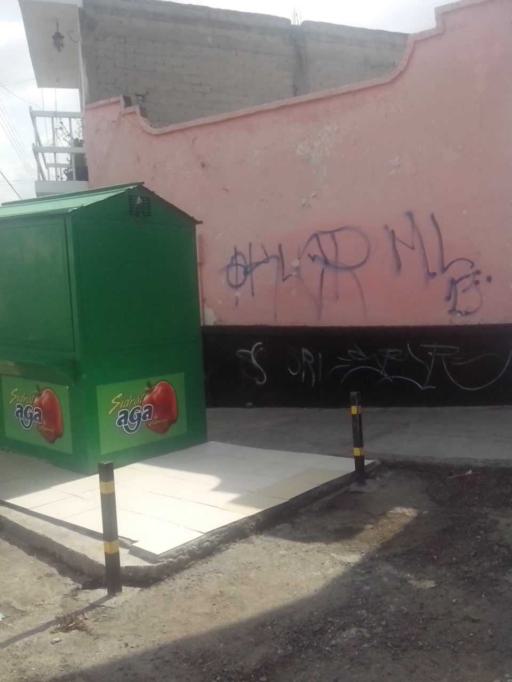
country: MX
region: Queretaro
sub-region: Queretaro
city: Santiago de Queretaro
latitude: 20.6058
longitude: -100.3969
